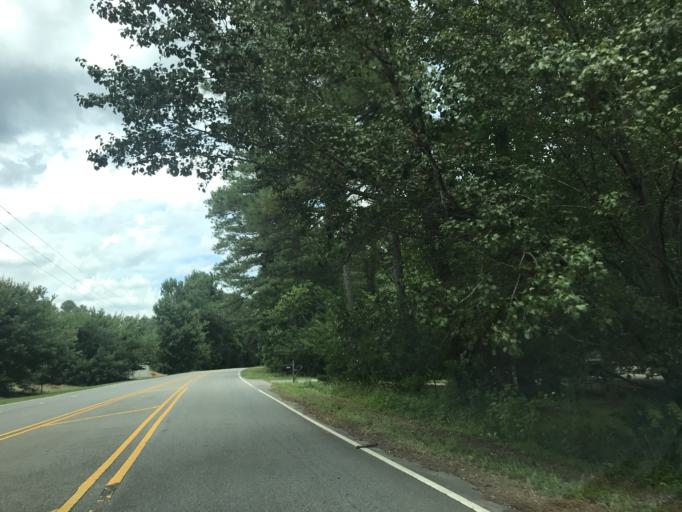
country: US
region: North Carolina
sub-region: Wake County
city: West Raleigh
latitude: 35.9103
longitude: -78.6966
